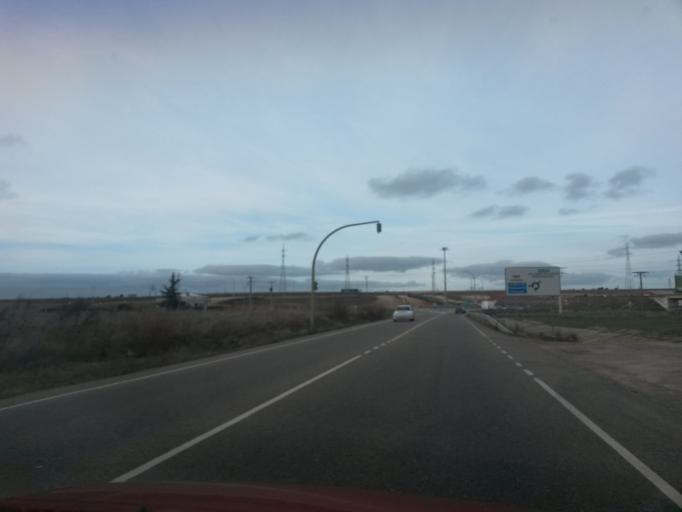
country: ES
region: Castille and Leon
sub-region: Provincia de Salamanca
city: Villares de la Reina
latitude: 40.9962
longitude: -5.6573
